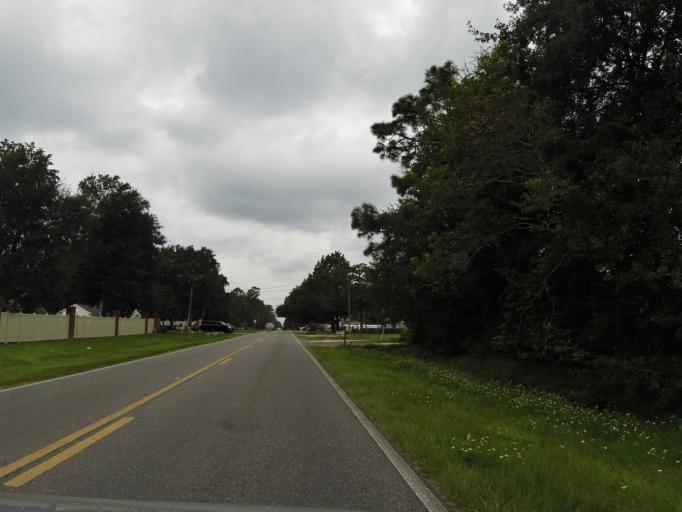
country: US
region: Florida
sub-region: Clay County
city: Middleburg
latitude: 30.1143
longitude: -81.8465
